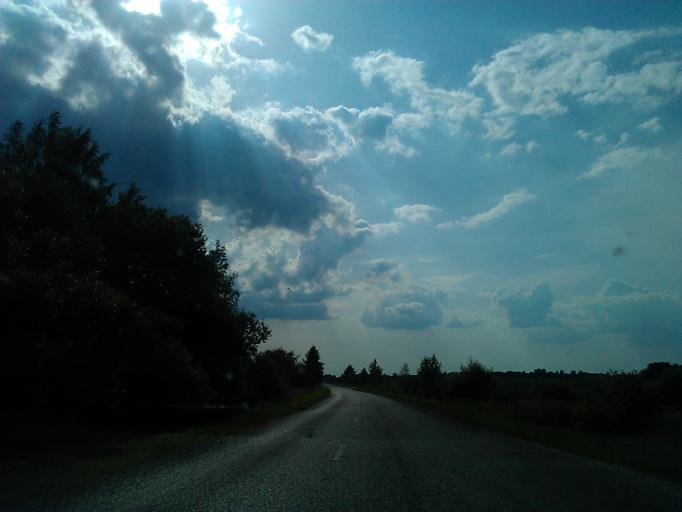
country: LV
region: Aizpute
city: Aizpute
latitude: 56.6991
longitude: 21.8003
